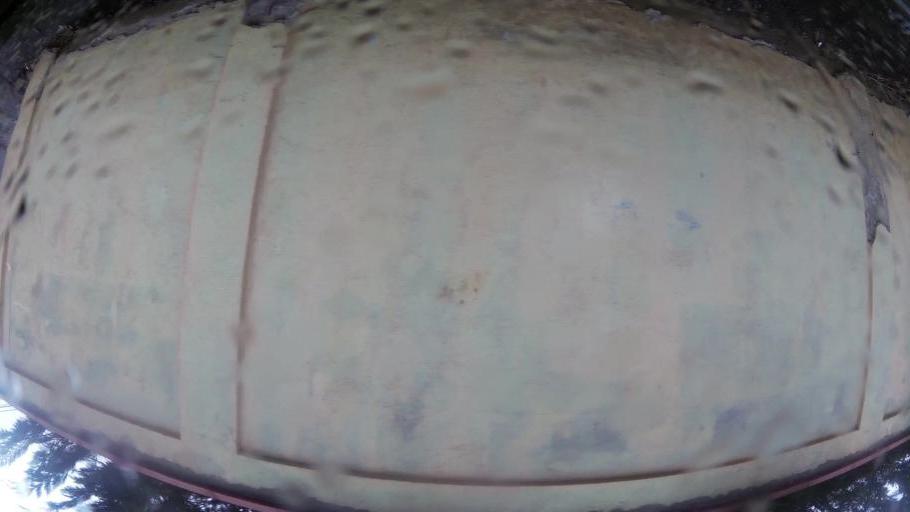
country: RO
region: Ilfov
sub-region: Comuna Bragadiru
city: Bragadiru
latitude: 44.4028
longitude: 26.0122
